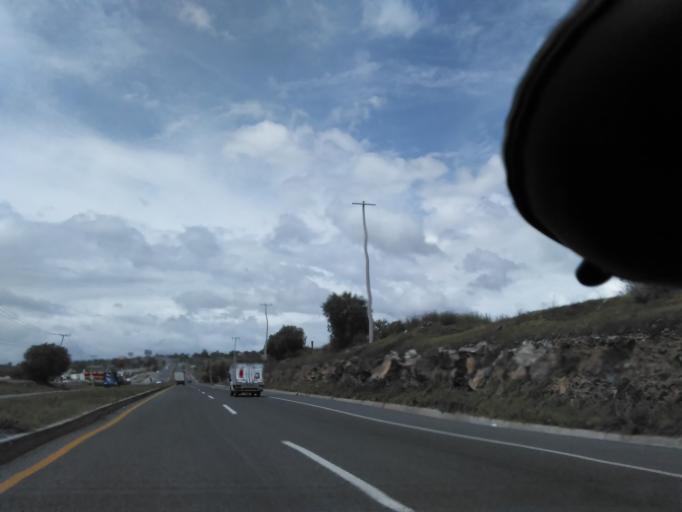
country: MX
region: Hidalgo
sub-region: Atotonilco de Tula
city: Paseos de la Pradera
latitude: 19.9213
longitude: -99.2379
